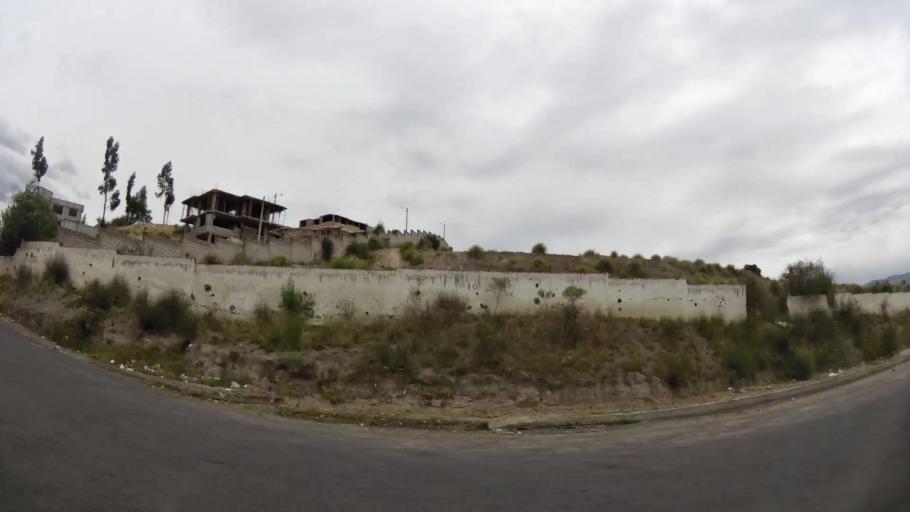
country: EC
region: Cotopaxi
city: Latacunga
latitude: -0.9492
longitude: -78.6047
